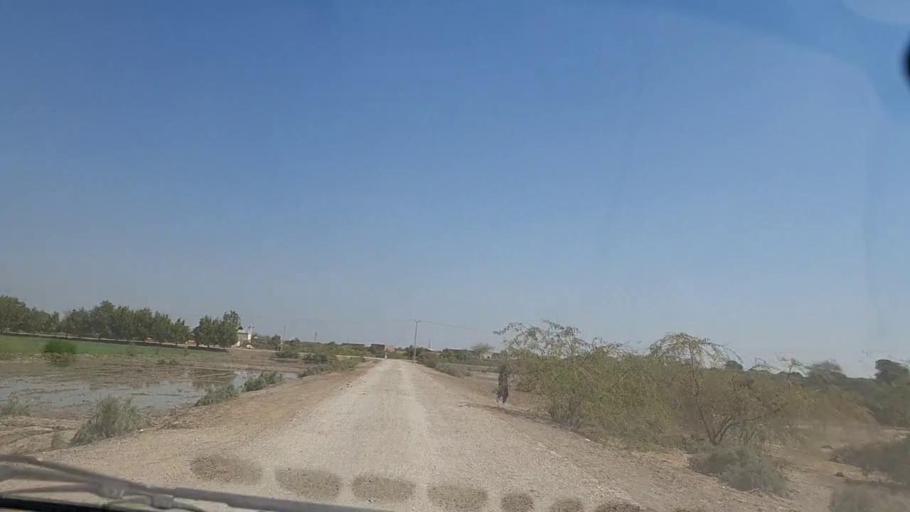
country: PK
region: Sindh
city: Mirpur Khas
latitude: 25.4256
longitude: 69.0422
